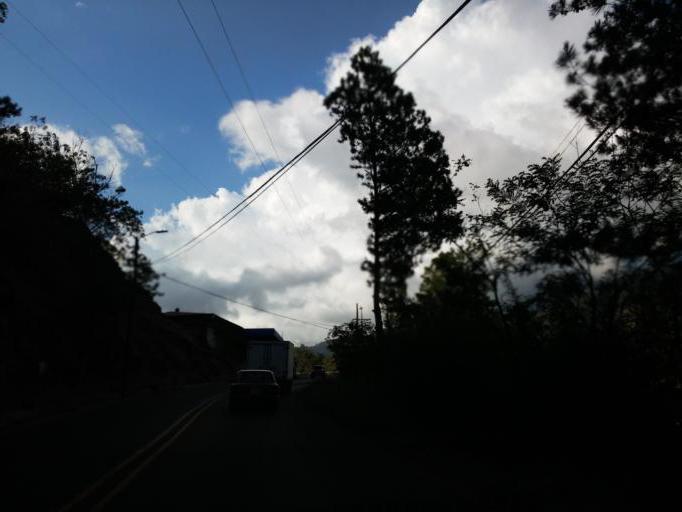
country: CR
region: San Jose
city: San Ignacio
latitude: 9.7972
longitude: -84.1571
